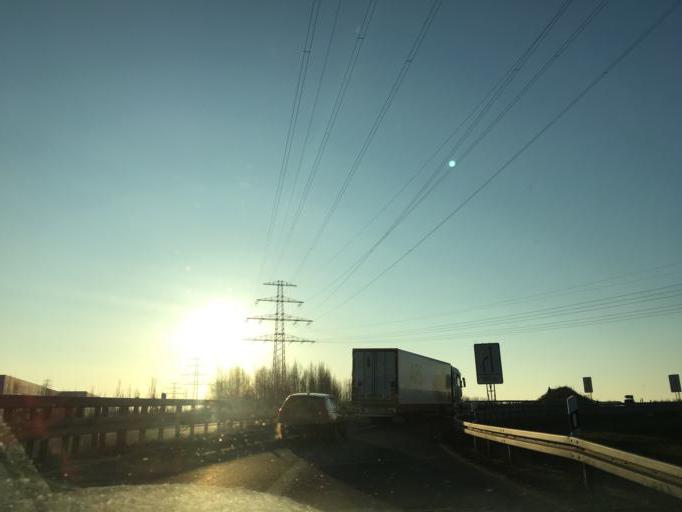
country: DE
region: Saxony
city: Taucha
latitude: 51.3702
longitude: 12.4708
